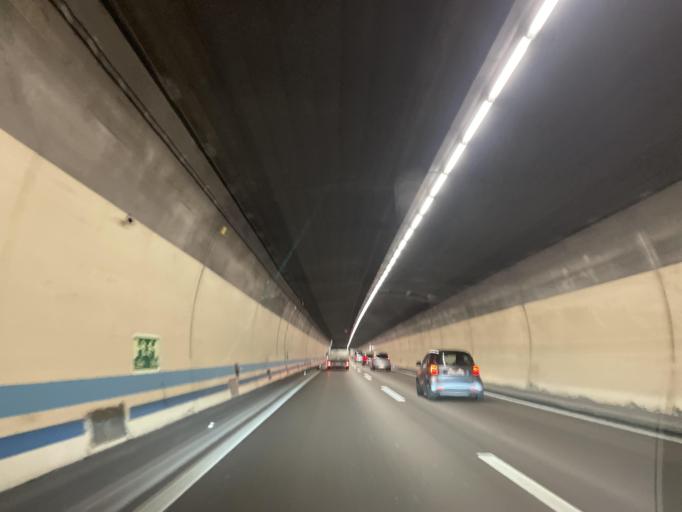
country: CH
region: Zurich
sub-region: Bezirk Dietikon
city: Birmensdorf
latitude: 47.3513
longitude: 8.4459
